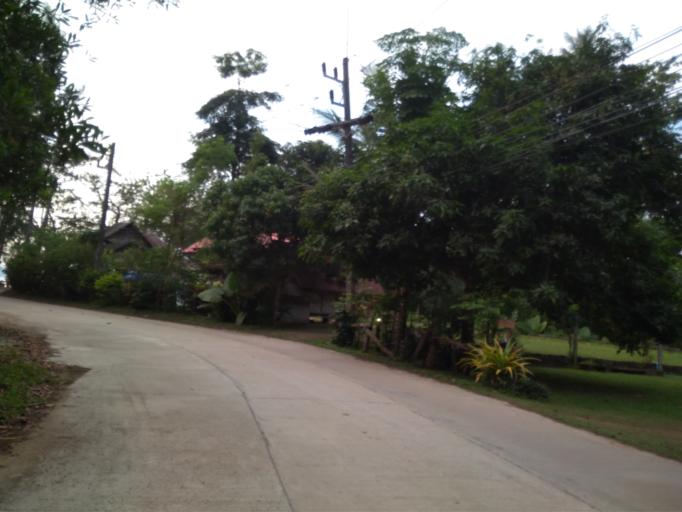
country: TH
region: Phangnga
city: Ko Yao
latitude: 8.1031
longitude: 98.6230
